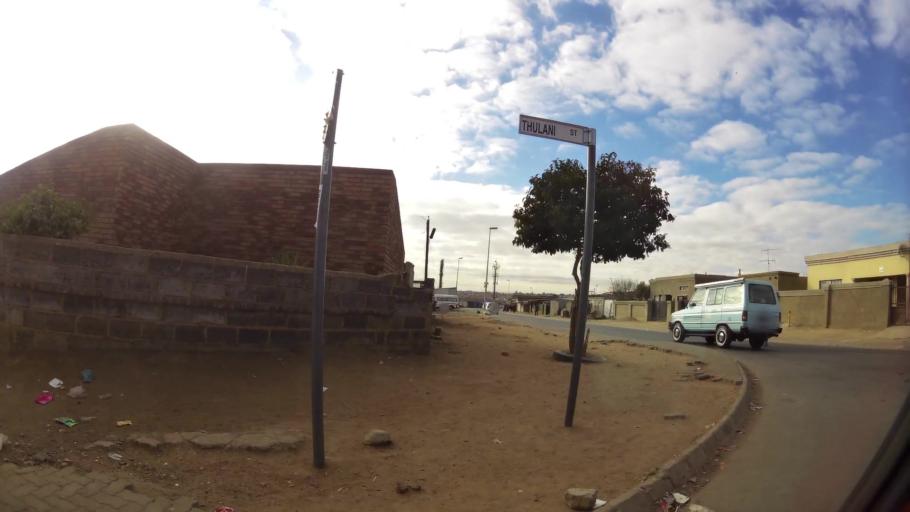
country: ZA
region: Gauteng
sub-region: City of Johannesburg Metropolitan Municipality
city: Modderfontein
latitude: -26.0385
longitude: 28.1846
